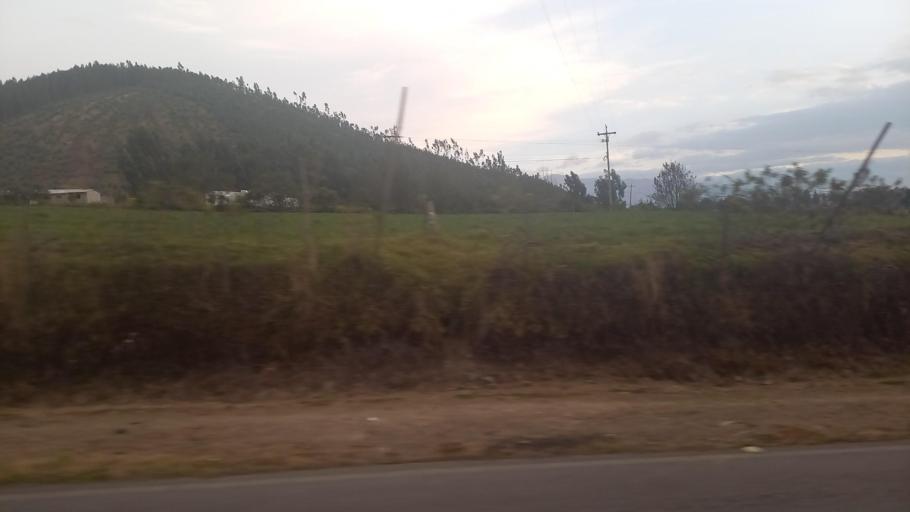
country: EC
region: Pichincha
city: Cayambe
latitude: 0.0705
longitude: -78.1158
